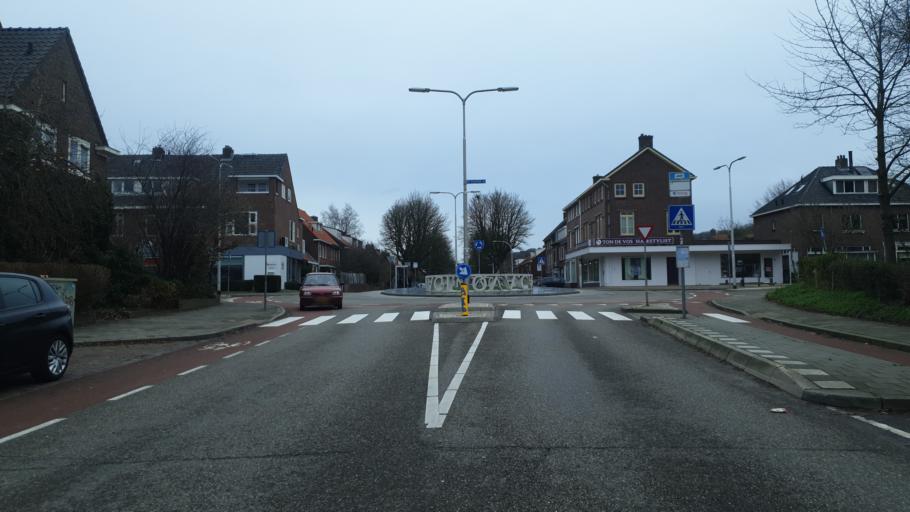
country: NL
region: Gelderland
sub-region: Gemeente Nijmegen
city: Nijmegen
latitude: 51.8337
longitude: 5.8852
